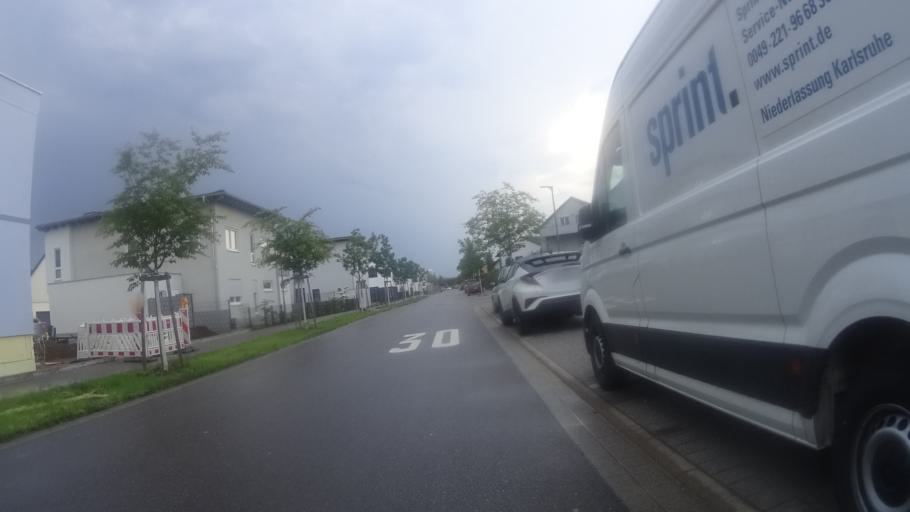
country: DE
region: Baden-Wuerttemberg
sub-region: Karlsruhe Region
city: Bietigheim
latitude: 48.9066
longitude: 8.2516
